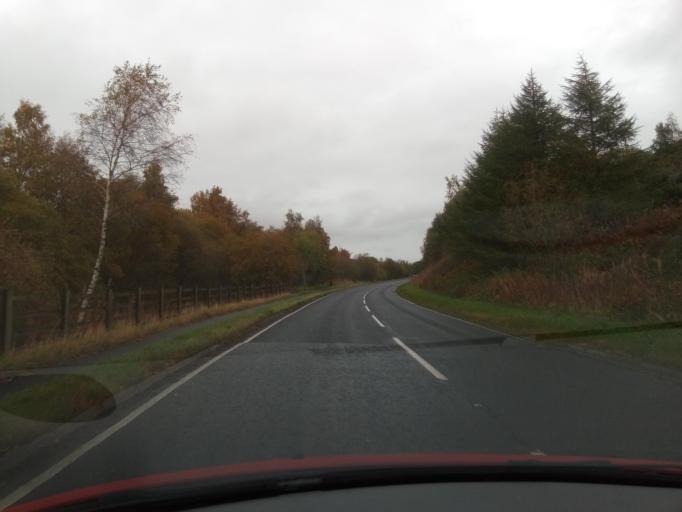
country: GB
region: Scotland
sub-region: The Scottish Borders
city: Galashiels
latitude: 55.6229
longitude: -2.8664
